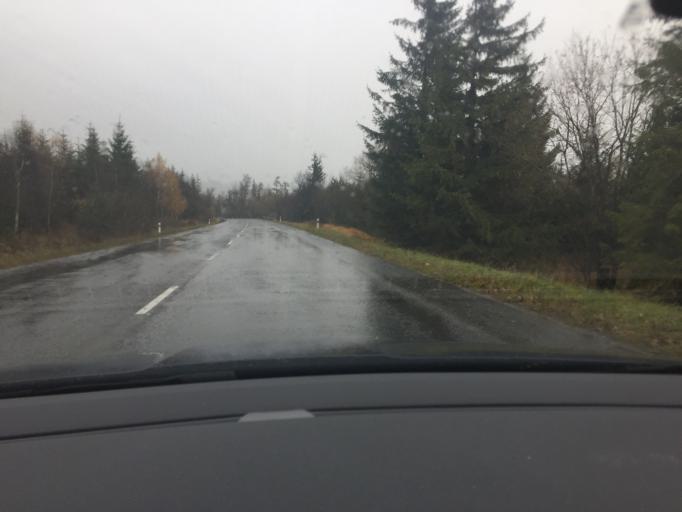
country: SK
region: Presovsky
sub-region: Okres Poprad
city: Zdiar
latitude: 49.1991
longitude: 20.3049
